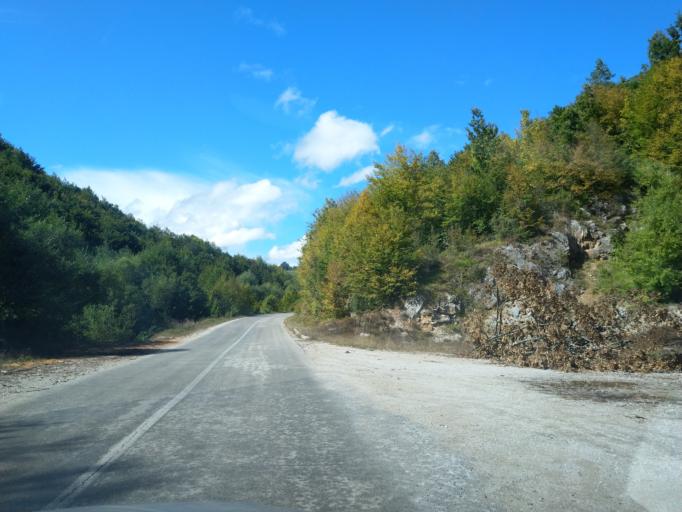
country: RS
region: Central Serbia
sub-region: Zlatiborski Okrug
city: Cajetina
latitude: 43.7109
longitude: 19.8377
